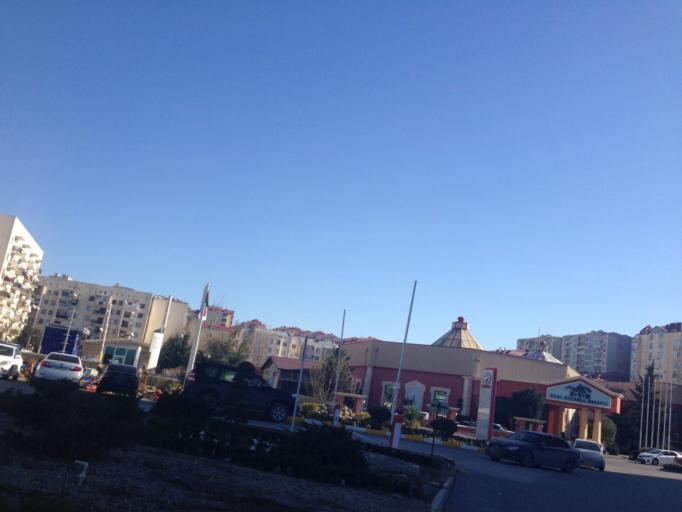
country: AZ
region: Baki
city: Baku
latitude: 40.3856
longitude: 49.8676
